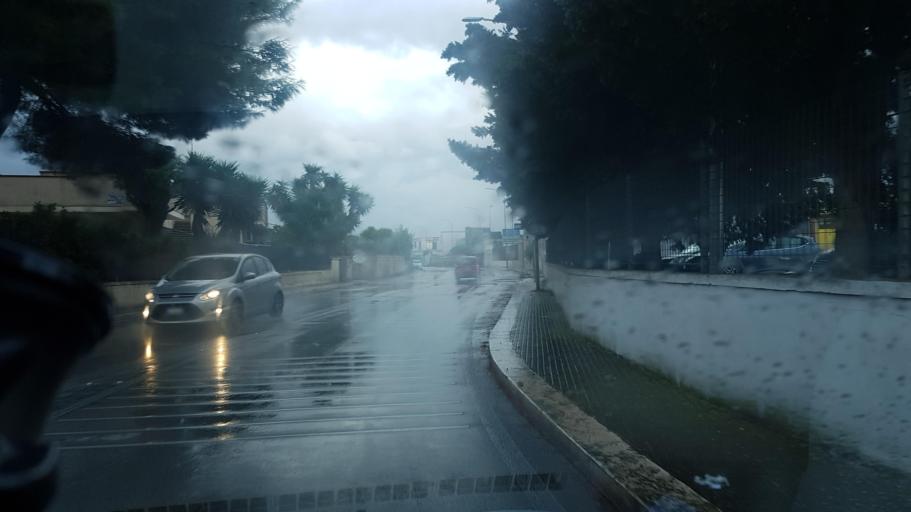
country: IT
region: Apulia
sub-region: Provincia di Lecce
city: Surbo
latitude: 40.3821
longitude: 18.1369
